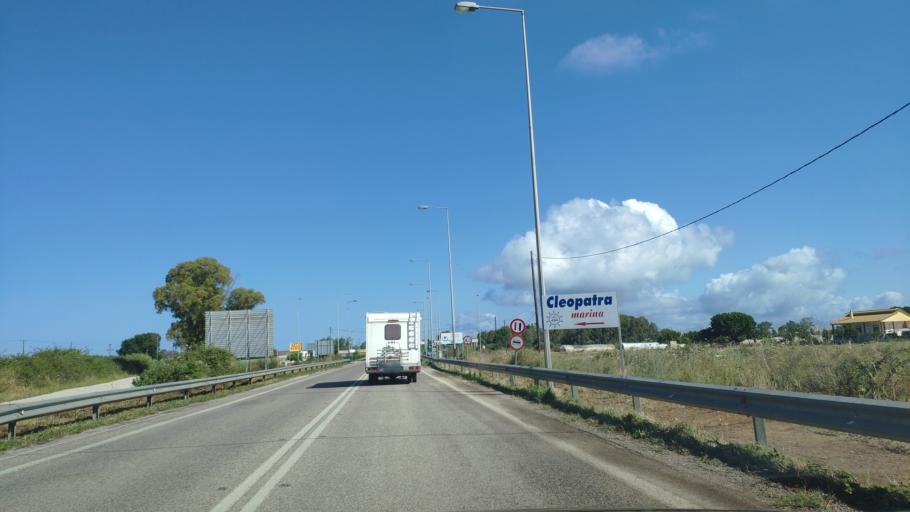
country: GR
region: Epirus
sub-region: Nomos Prevezis
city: Preveza
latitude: 38.9367
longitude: 20.7688
